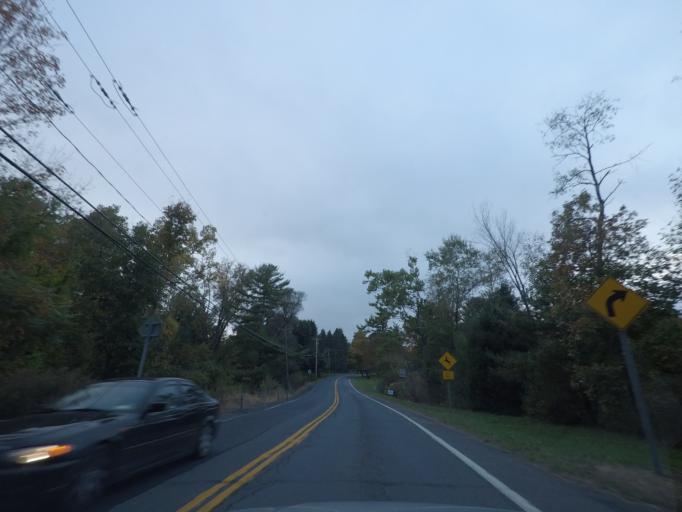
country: US
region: New York
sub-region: Rensselaer County
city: Nassau
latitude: 42.5609
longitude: -73.6435
